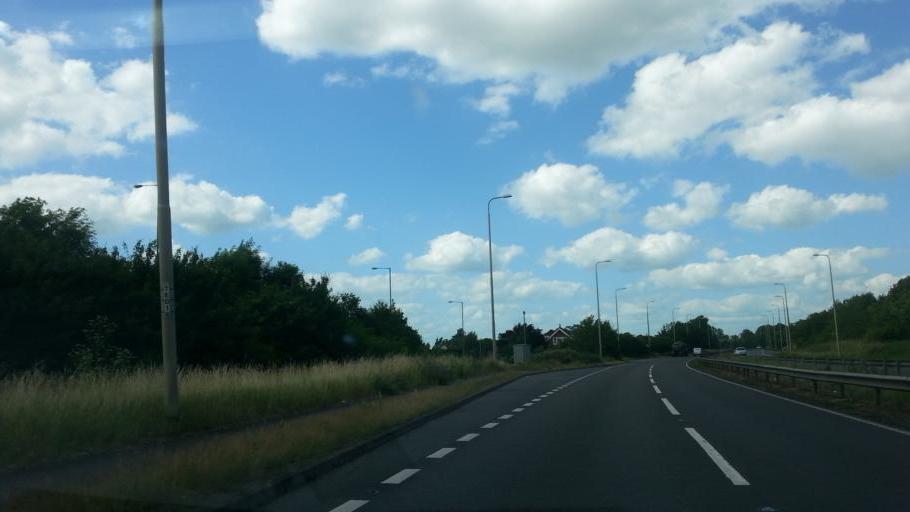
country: GB
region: England
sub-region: Central Bedfordshire
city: Tempsford
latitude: 52.1584
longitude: -0.3018
